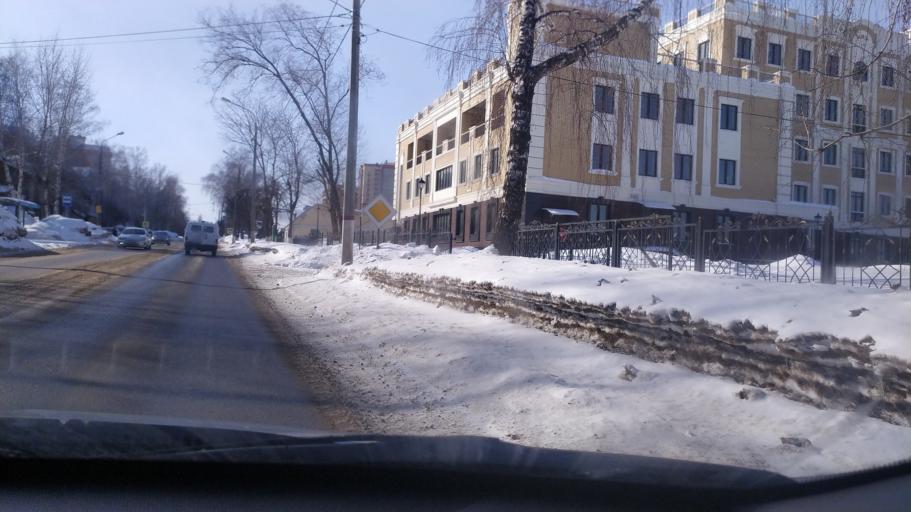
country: RU
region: Chuvashia
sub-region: Cheboksarskiy Rayon
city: Cheboksary
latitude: 56.1519
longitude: 47.2355
